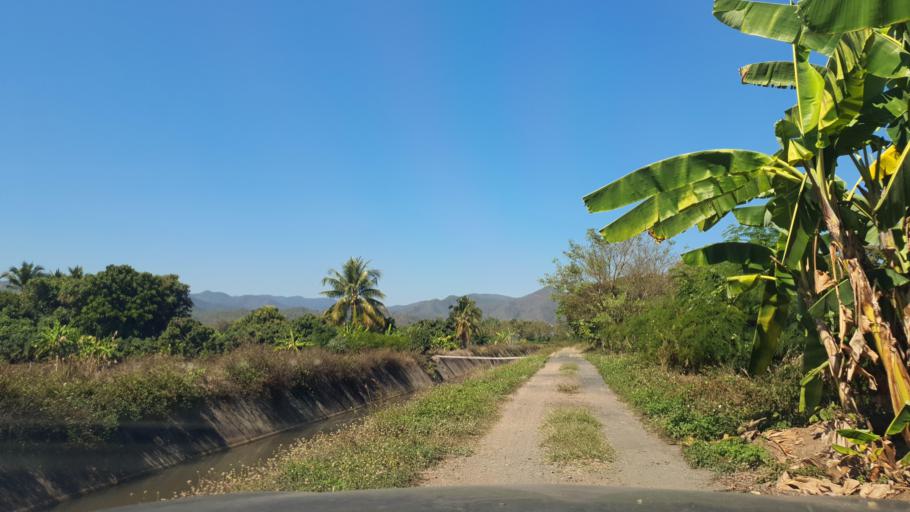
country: TH
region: Chiang Mai
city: Mae Wang
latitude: 18.6741
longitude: 98.8241
